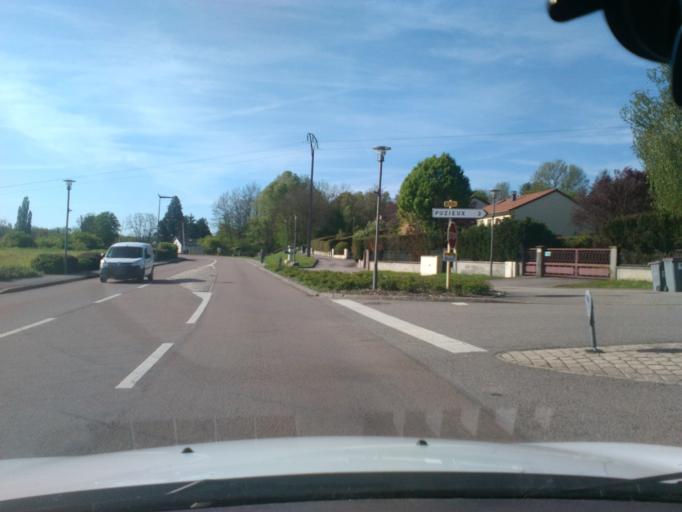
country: FR
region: Lorraine
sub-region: Departement des Vosges
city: Mirecourt
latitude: 48.3153
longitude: 6.1262
